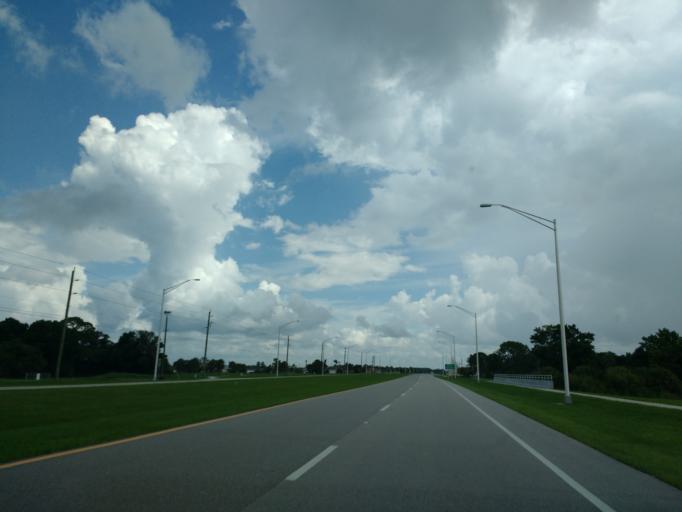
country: US
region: Florida
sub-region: Lee County
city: Burnt Store Marina
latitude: 26.7832
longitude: -82.0379
